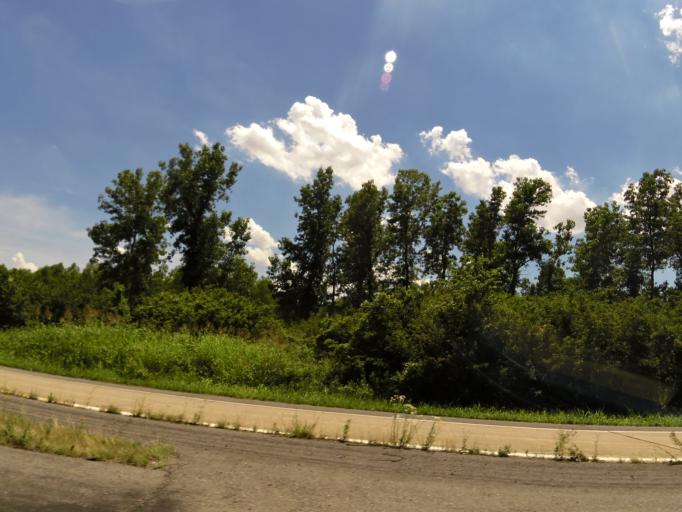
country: US
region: Missouri
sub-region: Pemiscot County
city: Caruthersville
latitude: 36.1529
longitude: -89.6668
